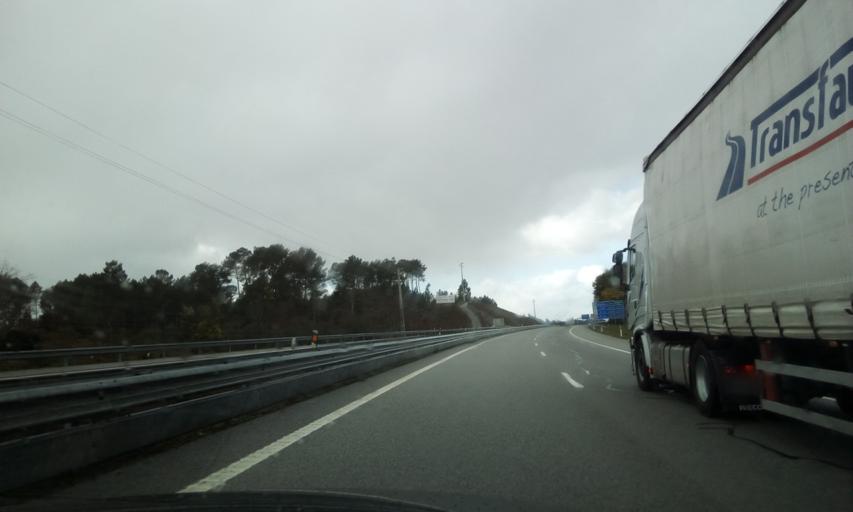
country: PT
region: Viseu
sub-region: Mangualde
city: Mangualde
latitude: 40.6156
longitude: -7.7521
